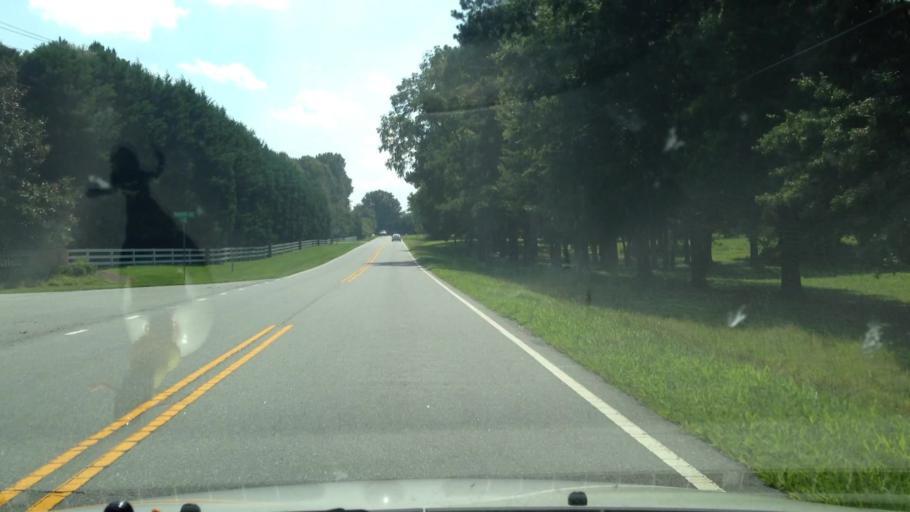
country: US
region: North Carolina
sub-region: Guilford County
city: Oak Ridge
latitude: 36.1665
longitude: -79.9993
